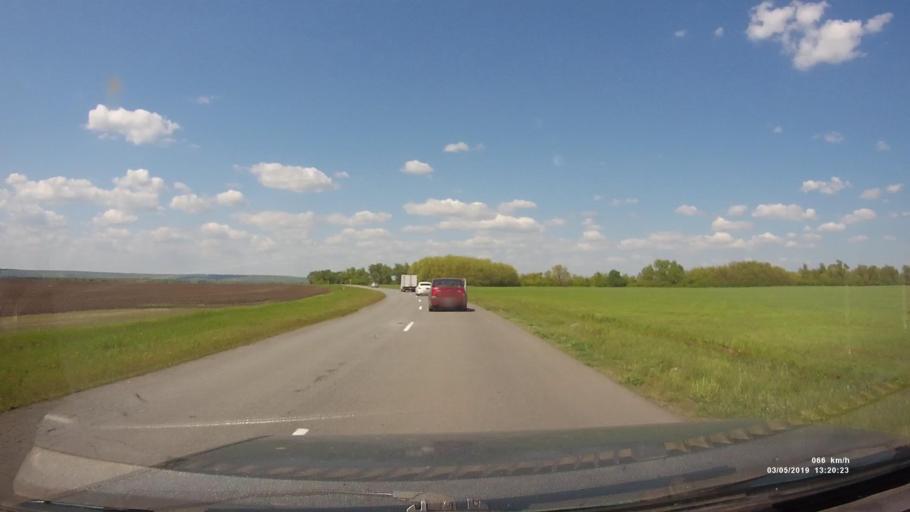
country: RU
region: Rostov
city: Semikarakorsk
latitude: 47.5457
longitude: 40.7539
